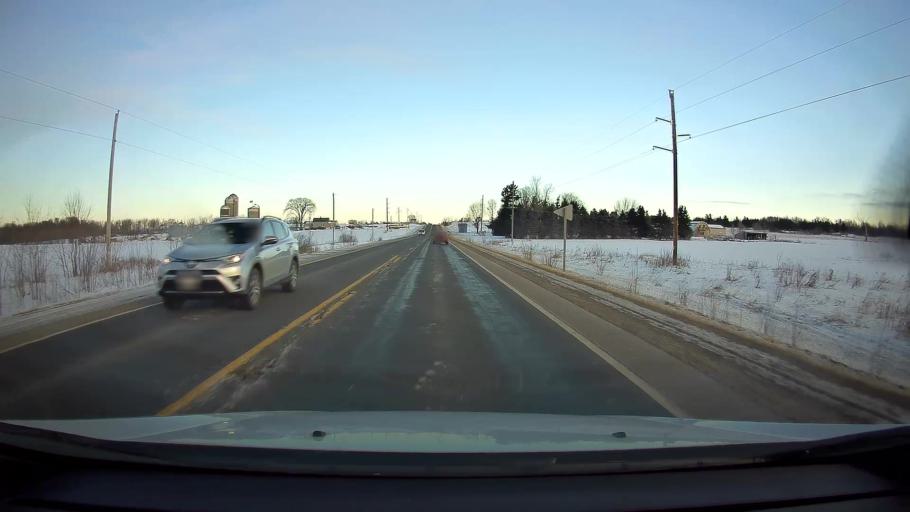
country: US
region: Wisconsin
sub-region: Barron County
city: Turtle Lake
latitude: 45.3647
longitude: -92.1668
